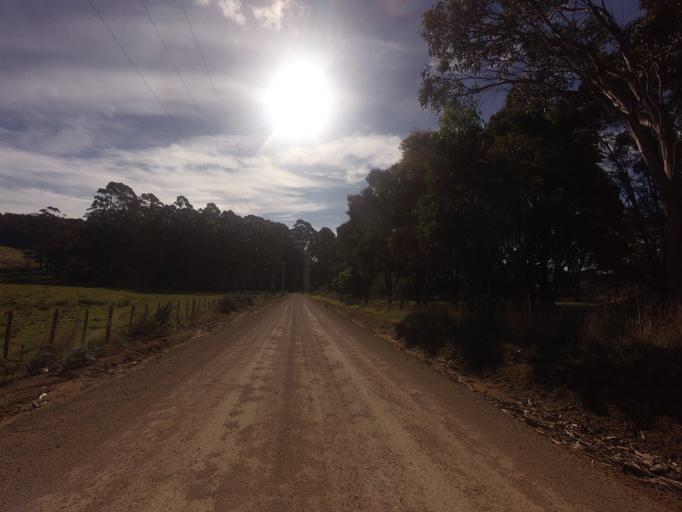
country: AU
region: Tasmania
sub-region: Clarence
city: Sandford
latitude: -43.1542
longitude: 147.7639
